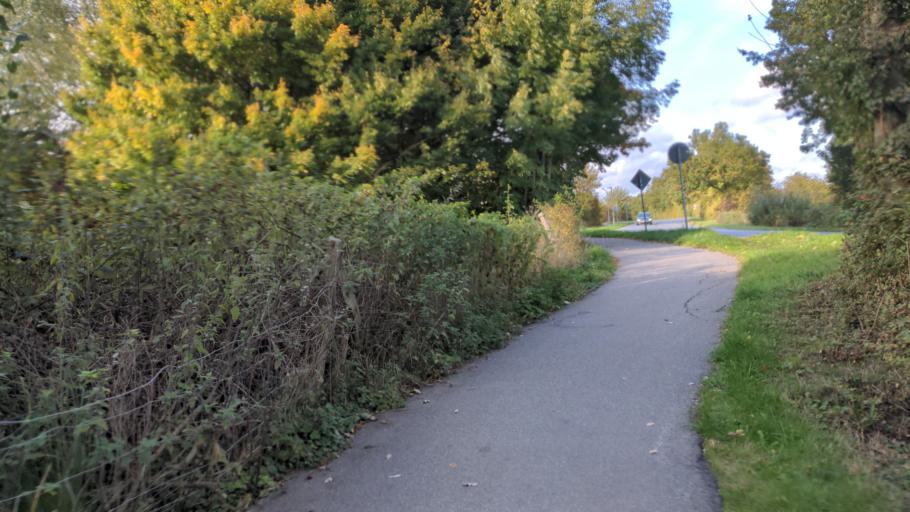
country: DE
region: Schleswig-Holstein
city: Ahrensbok
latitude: 54.0072
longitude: 10.5821
